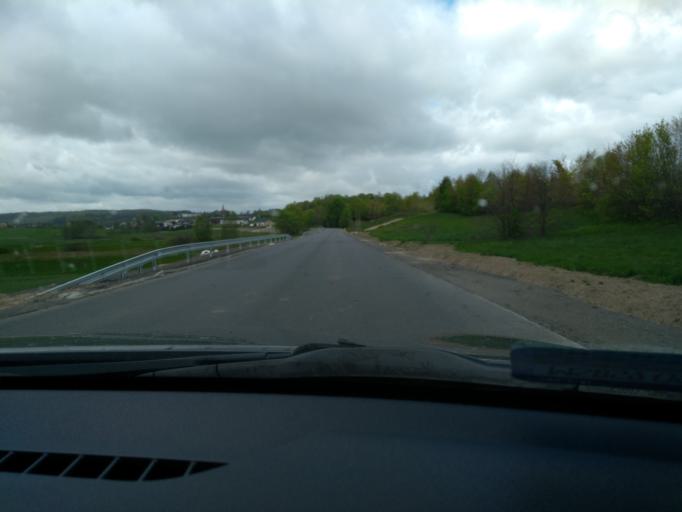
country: PL
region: Pomeranian Voivodeship
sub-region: Powiat kartuski
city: Chmielno
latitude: 54.3422
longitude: 18.0441
